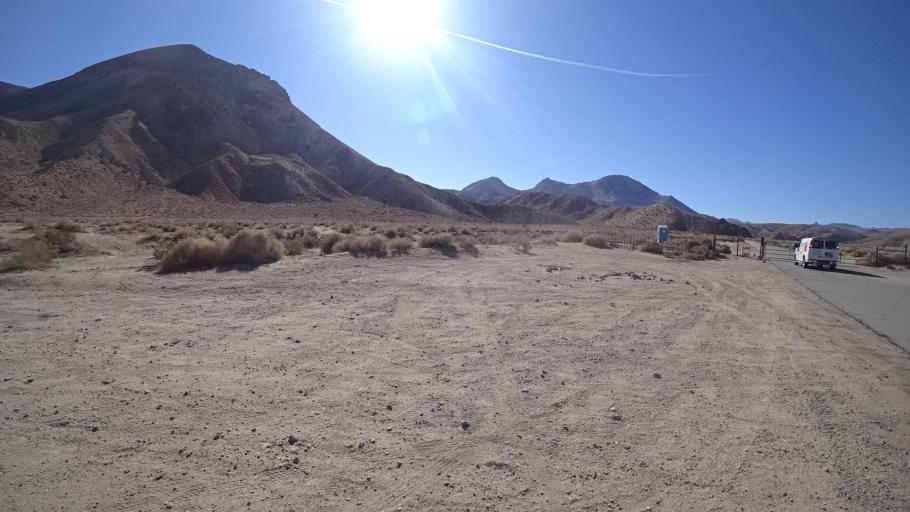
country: US
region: California
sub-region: Kern County
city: California City
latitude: 35.3080
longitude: -118.0992
